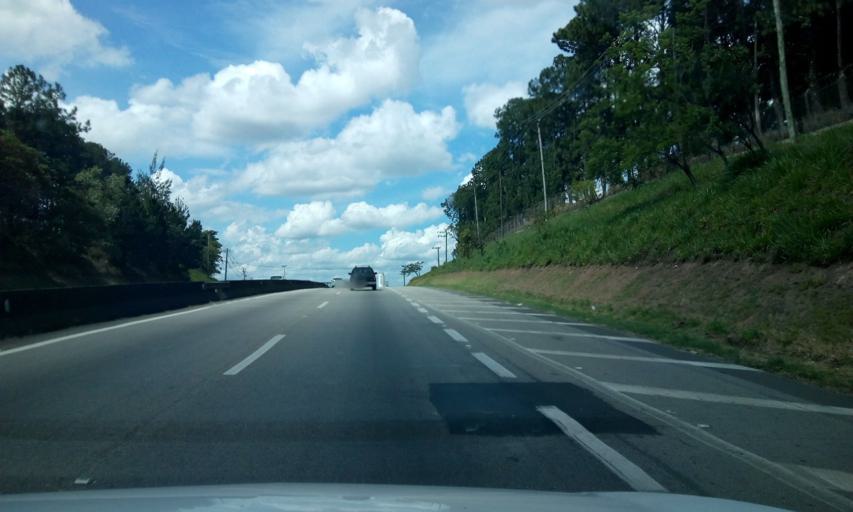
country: BR
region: Sao Paulo
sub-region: Jundiai
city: Jundiai
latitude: -23.1804
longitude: -46.9615
